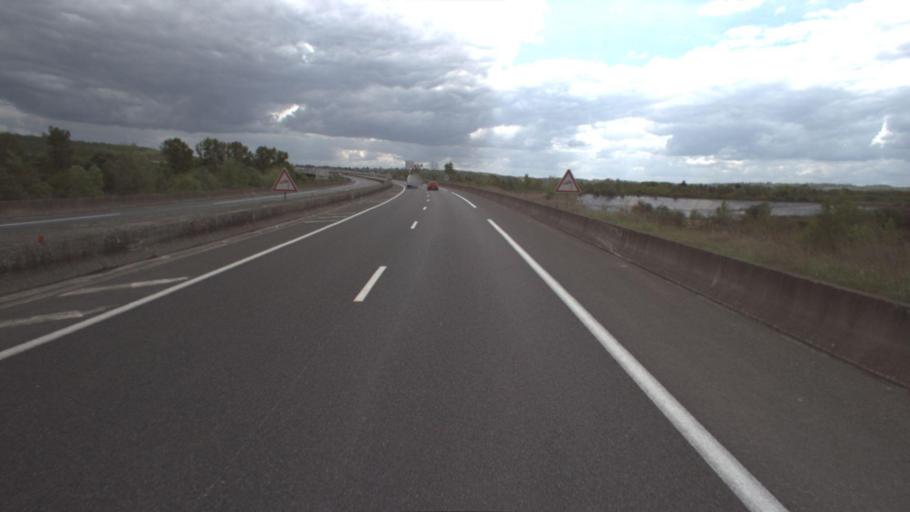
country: FR
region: Ile-de-France
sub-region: Departement de Seine-et-Marne
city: Mareuil-les-Meaux
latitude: 48.9242
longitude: 2.8449
